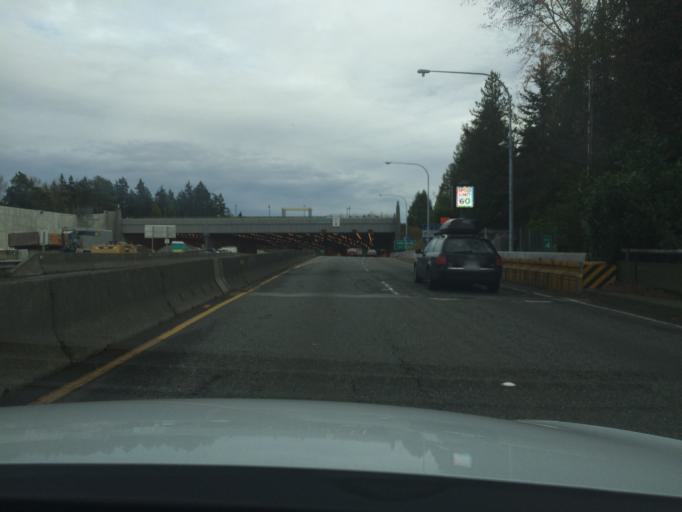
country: US
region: Washington
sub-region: King County
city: Medina
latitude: 47.6376
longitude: -122.2410
